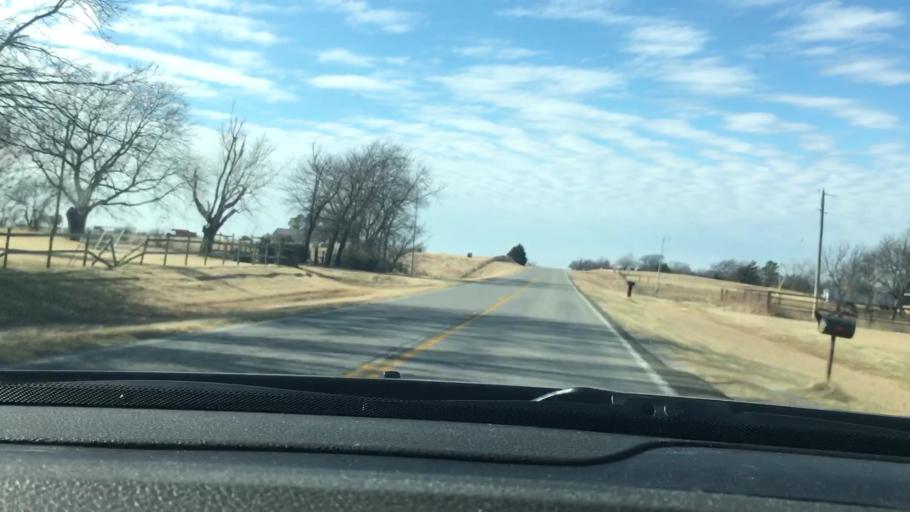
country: US
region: Oklahoma
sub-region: Garvin County
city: Wynnewood
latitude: 34.6515
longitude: -97.1022
